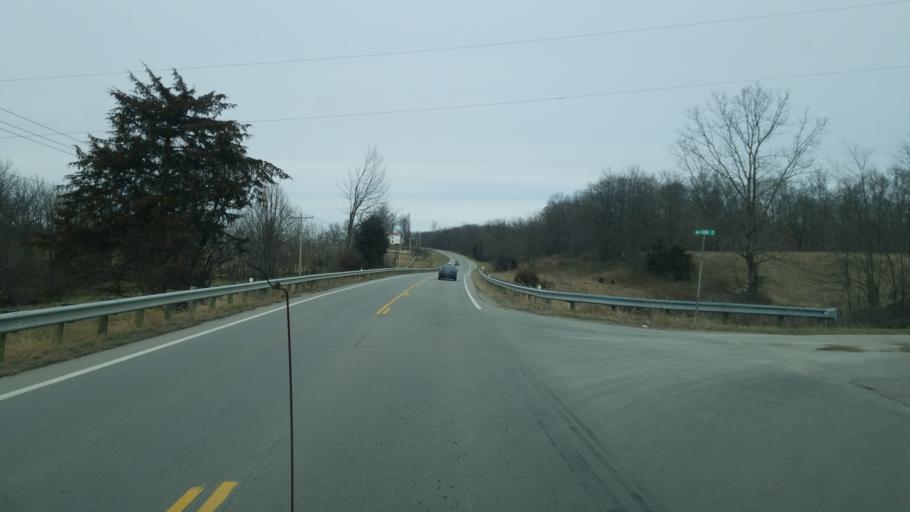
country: US
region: Ohio
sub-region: Adams County
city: Winchester
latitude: 39.0001
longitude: -83.7117
